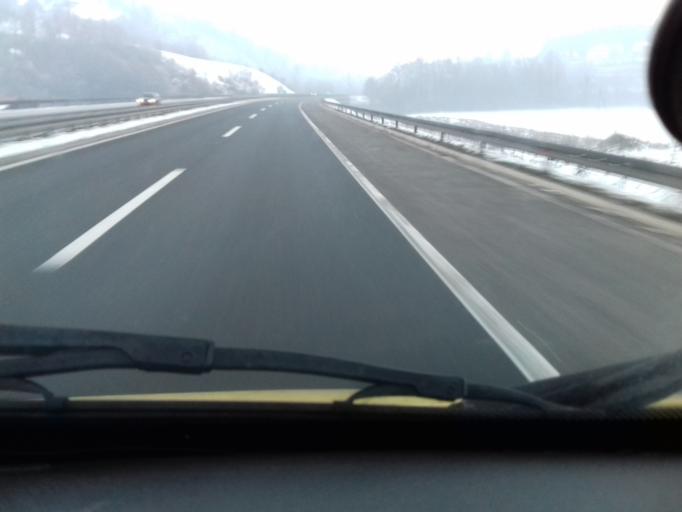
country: BA
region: Federation of Bosnia and Herzegovina
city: Vogosca
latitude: 43.9221
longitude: 18.3078
